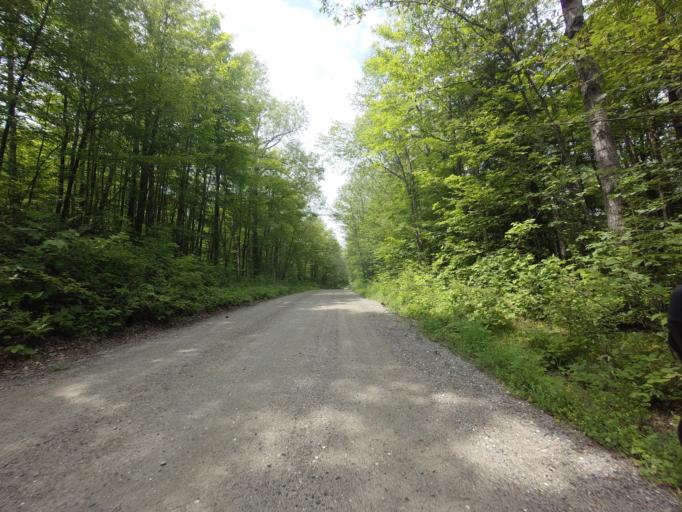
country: CA
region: Ontario
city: Perth
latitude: 44.7817
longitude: -76.6210
